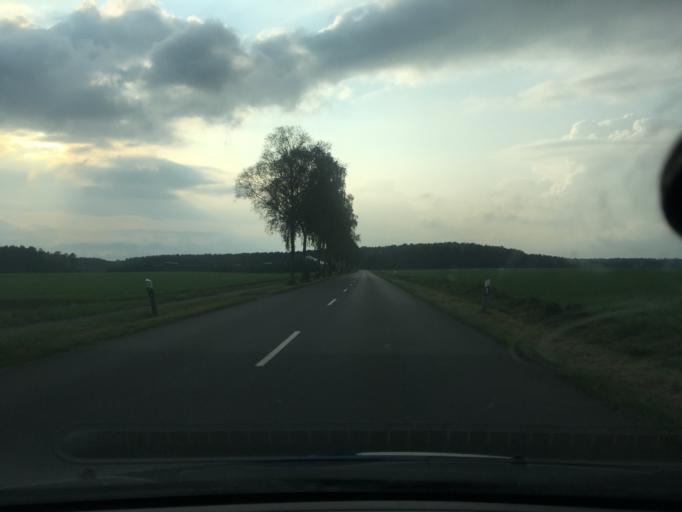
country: DE
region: Lower Saxony
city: Soderstorf
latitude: 53.1252
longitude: 10.1156
